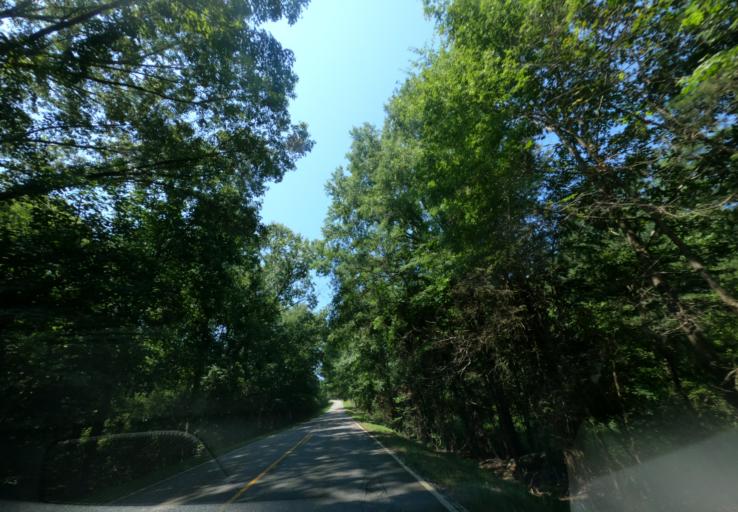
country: US
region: South Carolina
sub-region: McCormick County
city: McCormick
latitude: 34.0040
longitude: -82.1269
